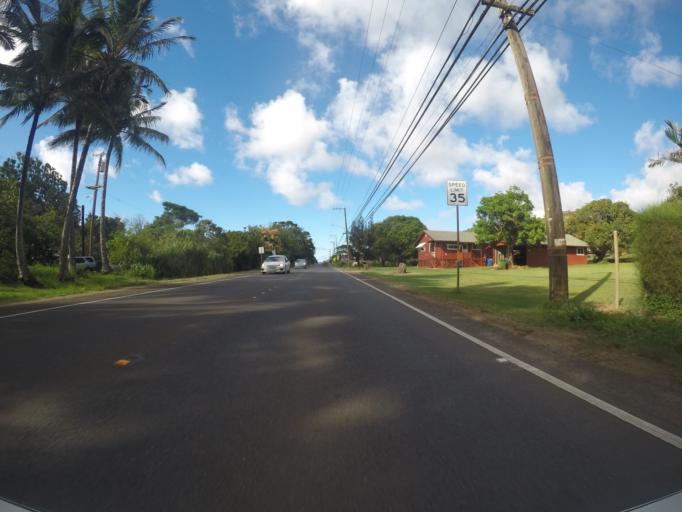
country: US
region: Hawaii
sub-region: Honolulu County
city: Pupukea
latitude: 21.6702
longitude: -158.0443
